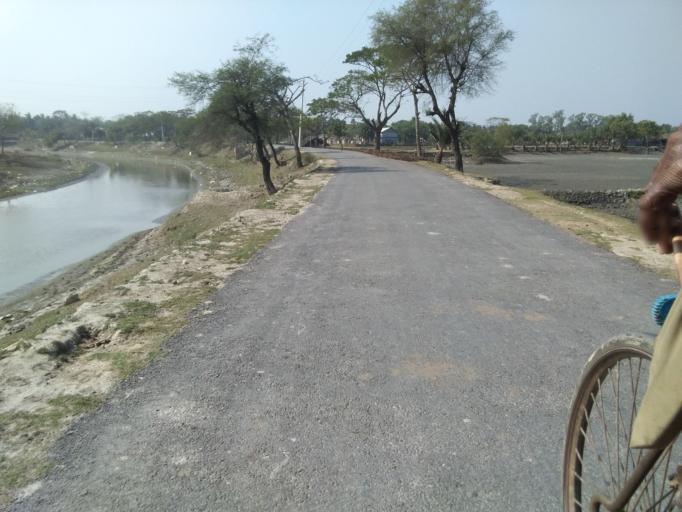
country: IN
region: West Bengal
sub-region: North 24 Parganas
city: Taki
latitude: 22.6366
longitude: 89.0039
